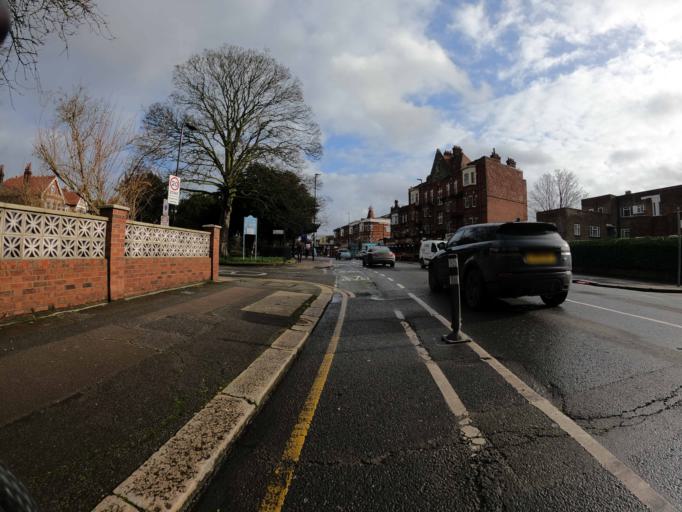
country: GB
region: England
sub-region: Greater London
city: Acton
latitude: 51.5088
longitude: -0.2833
